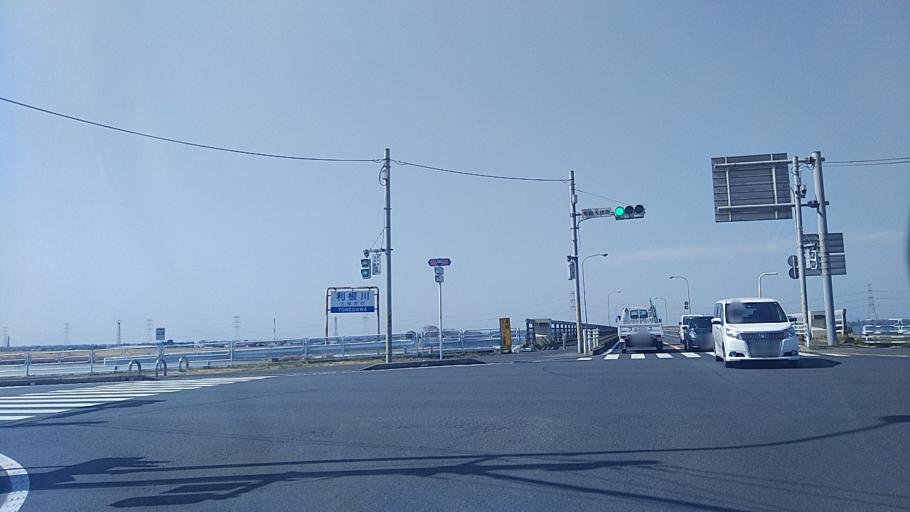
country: JP
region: Ibaraki
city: Edosaki
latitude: 35.8803
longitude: 140.3506
